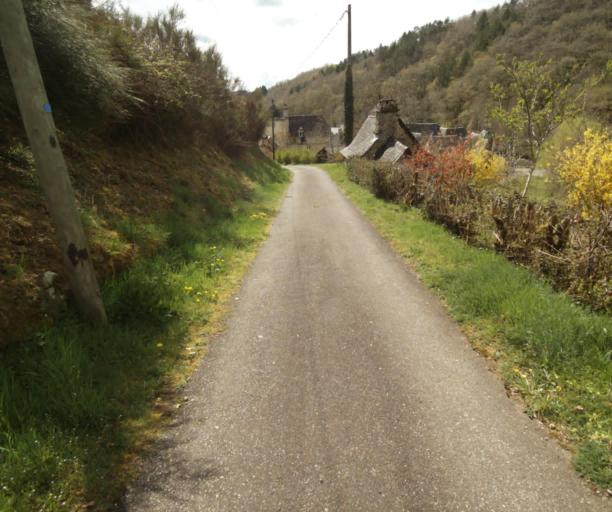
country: FR
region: Limousin
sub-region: Departement de la Correze
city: Argentat
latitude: 45.1768
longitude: 1.8763
